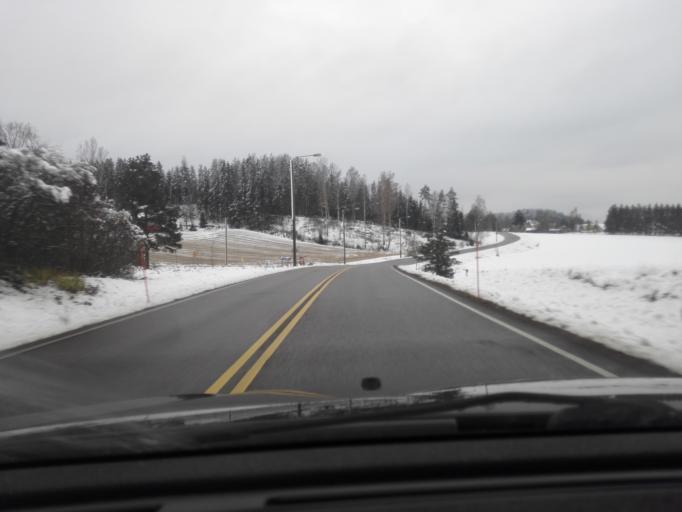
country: FI
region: Uusimaa
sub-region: Helsinki
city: Vihti
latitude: 60.4204
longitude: 24.3515
